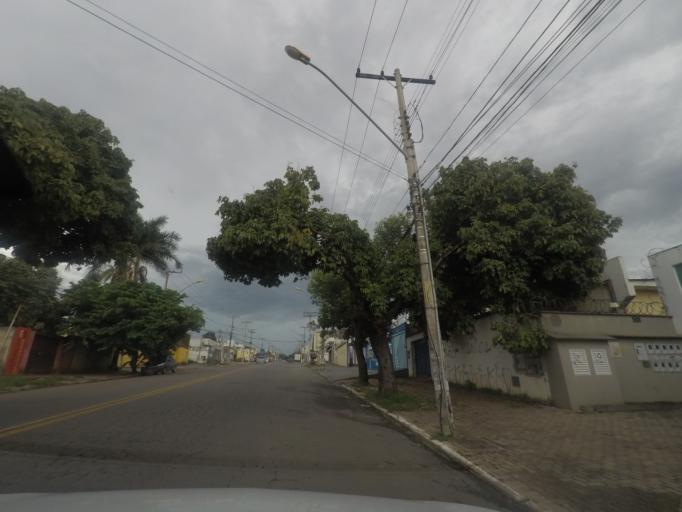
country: BR
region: Goias
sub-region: Goiania
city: Goiania
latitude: -16.6862
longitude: -49.2476
